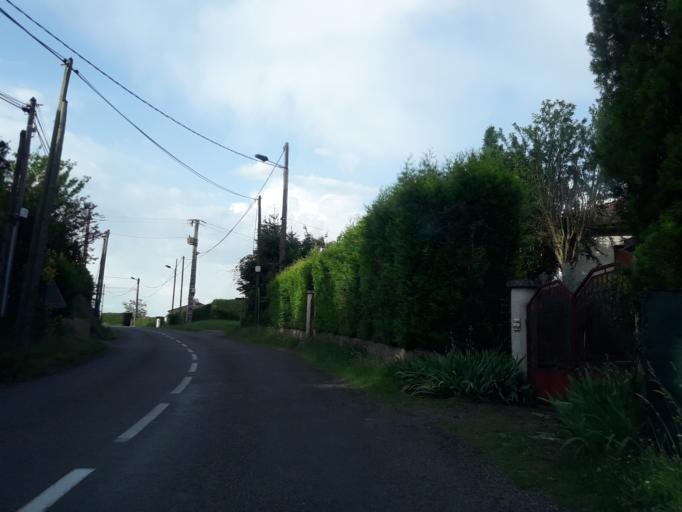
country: FR
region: Rhone-Alpes
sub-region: Departement du Rhone
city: Courzieu
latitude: 45.7503
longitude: 4.5420
